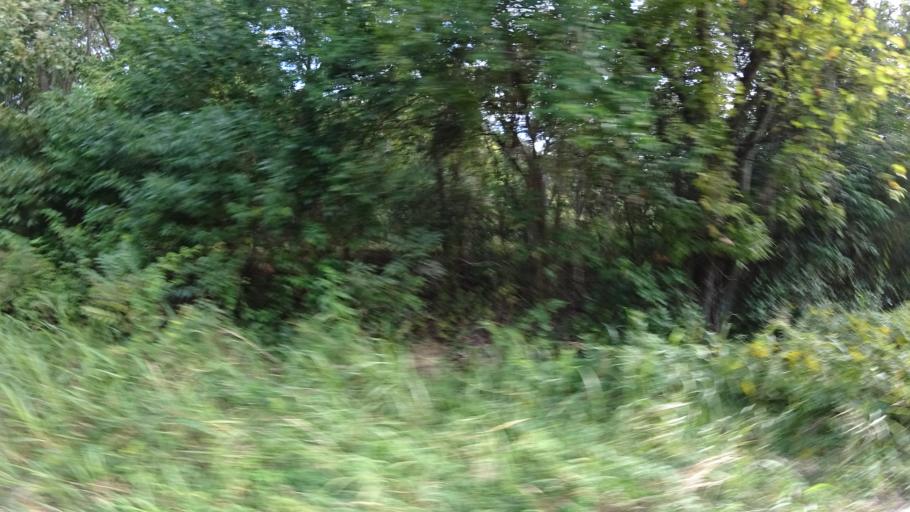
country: US
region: Texas
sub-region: Travis County
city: Austin
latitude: 30.2042
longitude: -97.7348
